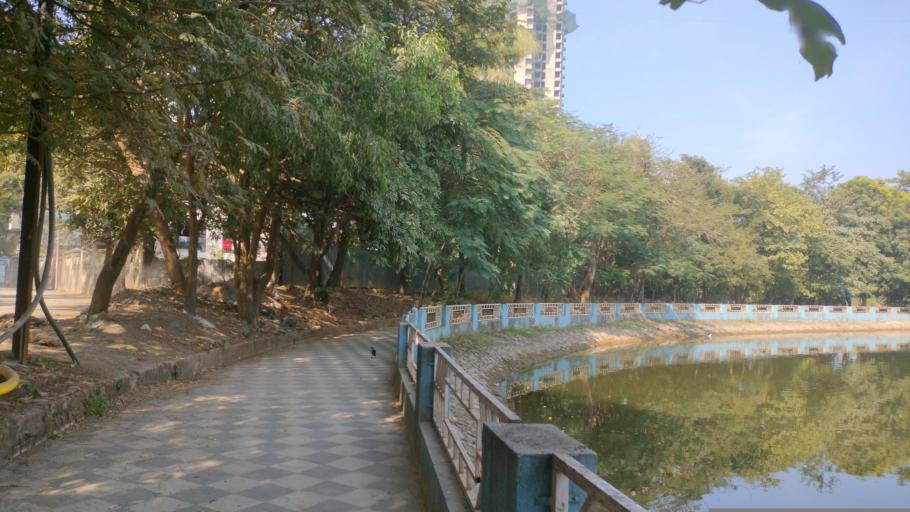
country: IN
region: Maharashtra
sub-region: Thane
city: Thane
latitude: 19.2760
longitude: 72.9652
